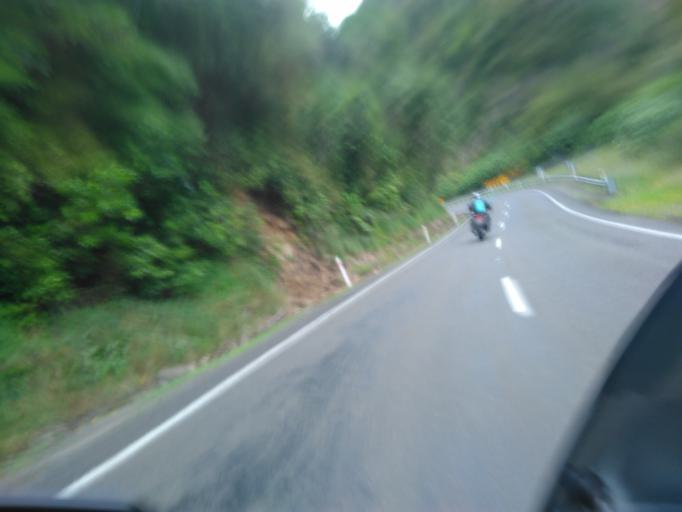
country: NZ
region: Bay of Plenty
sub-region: Opotiki District
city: Opotiki
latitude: -38.2962
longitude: 177.3913
